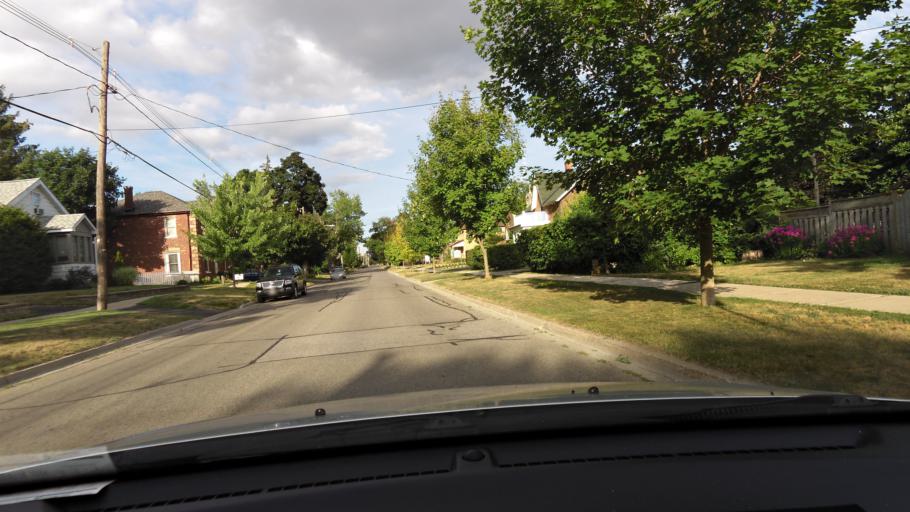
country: CA
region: Ontario
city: Angus
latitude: 44.1515
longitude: -79.8758
